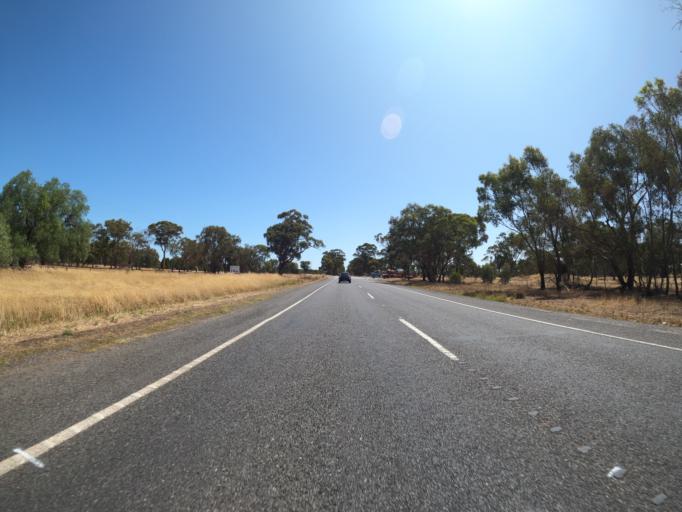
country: AU
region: New South Wales
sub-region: Corowa Shire
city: Corowa
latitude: -36.0611
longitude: 146.4109
